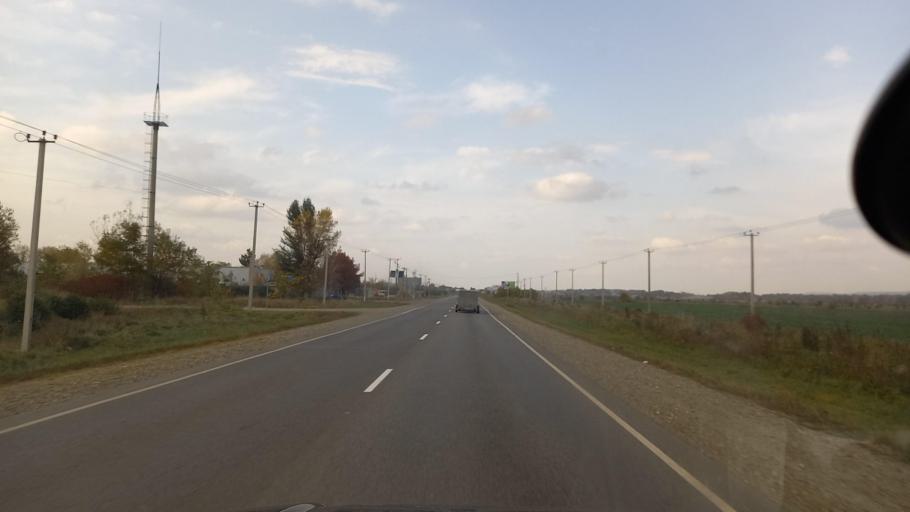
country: RU
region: Krasnodarskiy
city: Mostovskoy
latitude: 44.3805
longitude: 40.8216
